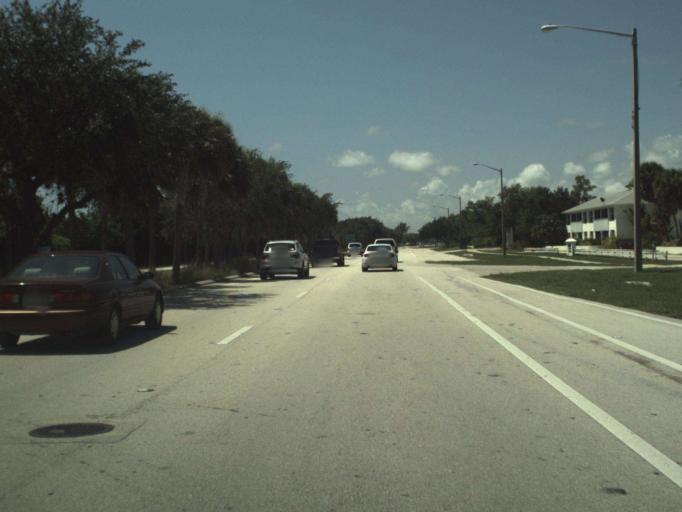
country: US
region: Florida
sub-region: Indian River County
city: Vero Beach
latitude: 27.6453
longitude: -80.3816
